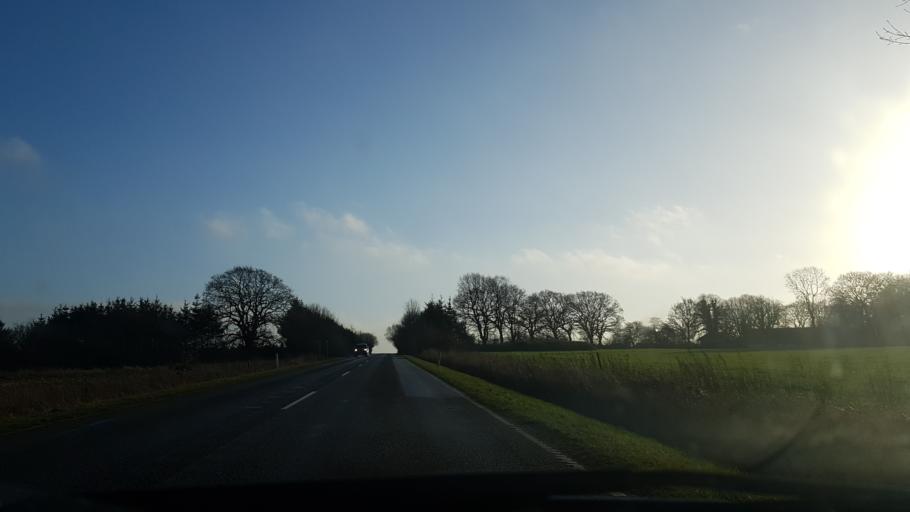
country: DK
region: South Denmark
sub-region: Tonder Kommune
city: Toftlund
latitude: 55.2200
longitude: 9.1801
